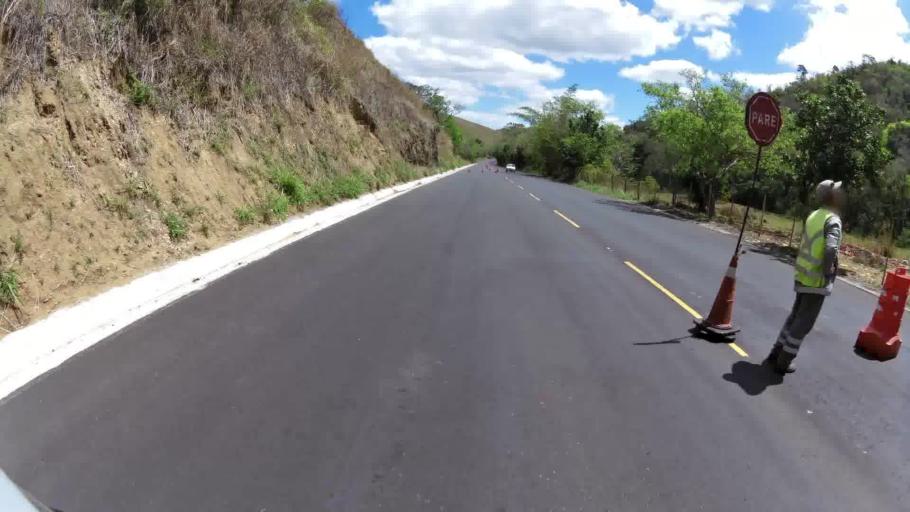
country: BR
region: Rio de Janeiro
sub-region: Itaperuna
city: Itaperuna
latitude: -21.2922
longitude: -41.8142
